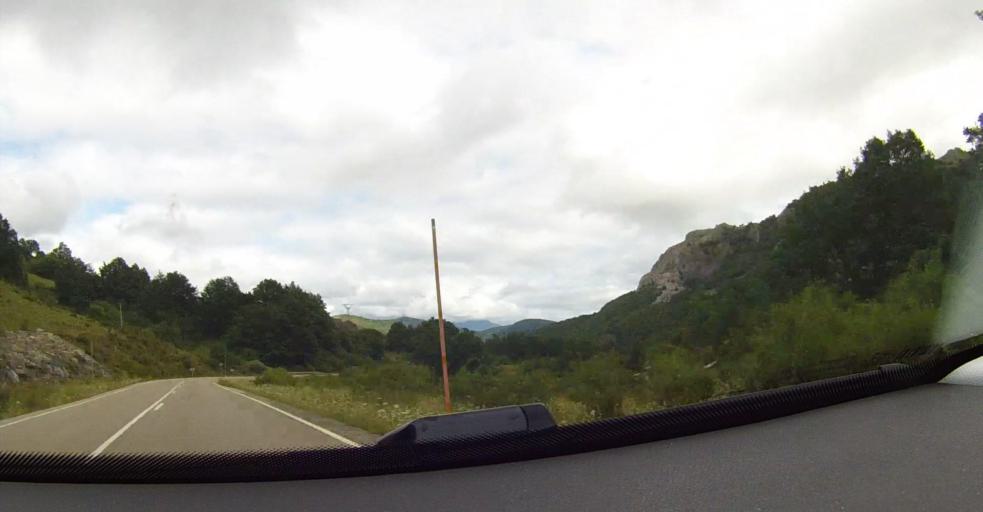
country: ES
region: Castille and Leon
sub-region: Provincia de Leon
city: Buron
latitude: 43.0168
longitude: -5.0283
